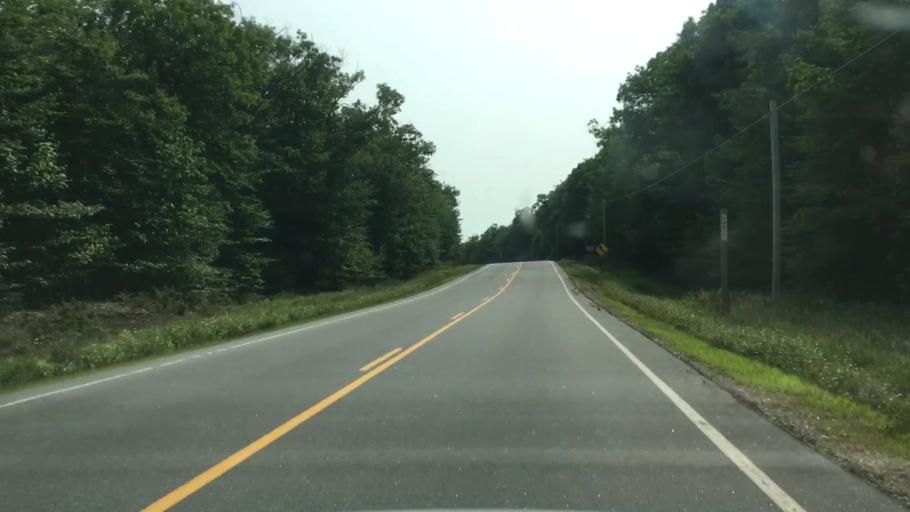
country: US
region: Maine
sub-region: Oxford County
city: Paris
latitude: 44.2598
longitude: -70.4370
